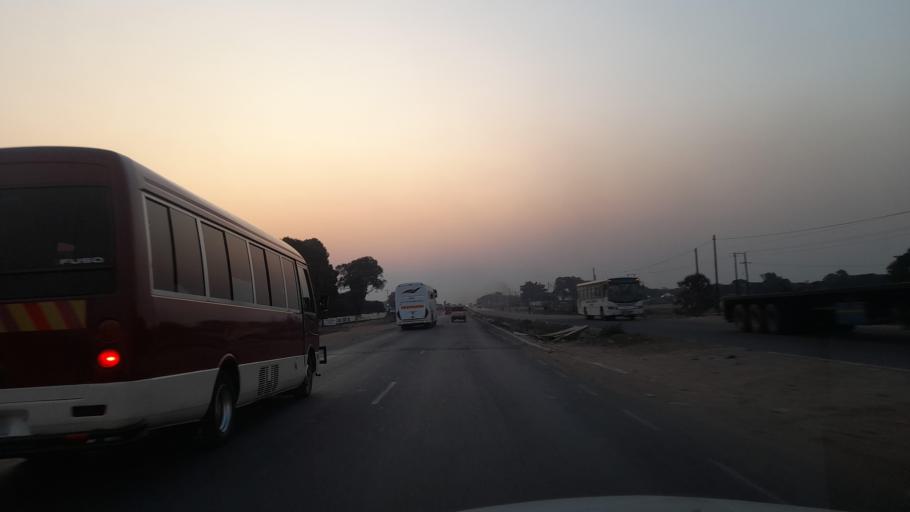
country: ZM
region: Copperbelt
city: Kitwe
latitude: -12.7735
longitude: 28.1880
